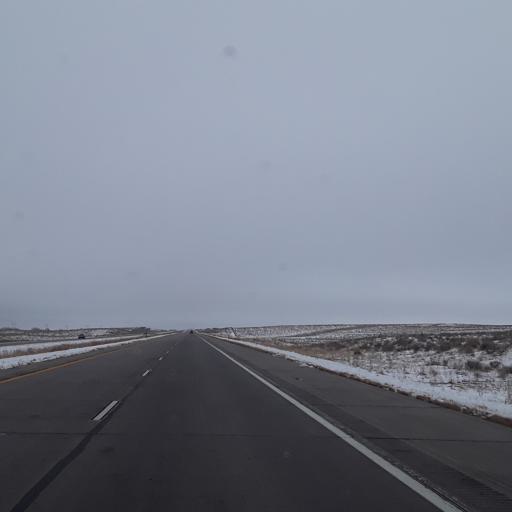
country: US
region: Colorado
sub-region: Logan County
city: Sterling
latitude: 40.5822
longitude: -103.1966
